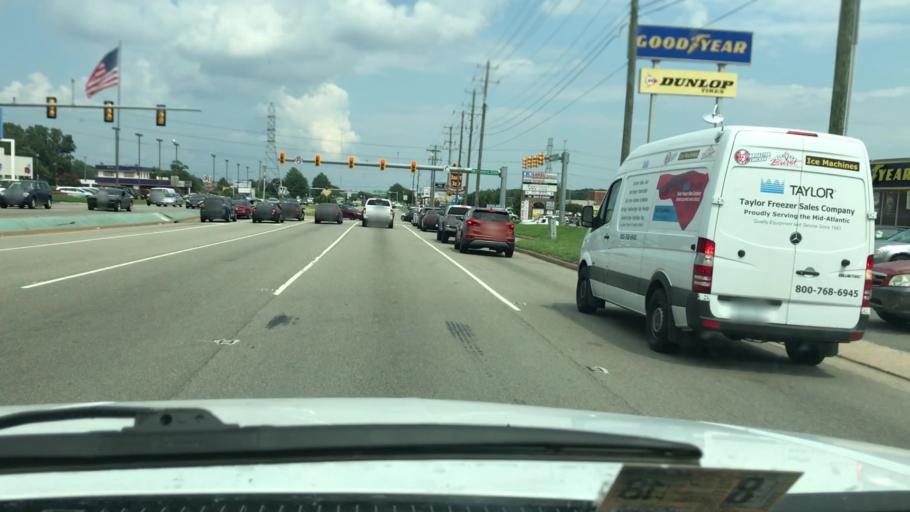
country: US
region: Virginia
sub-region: Chesterfield County
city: Bon Air
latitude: 37.4995
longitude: -77.5351
